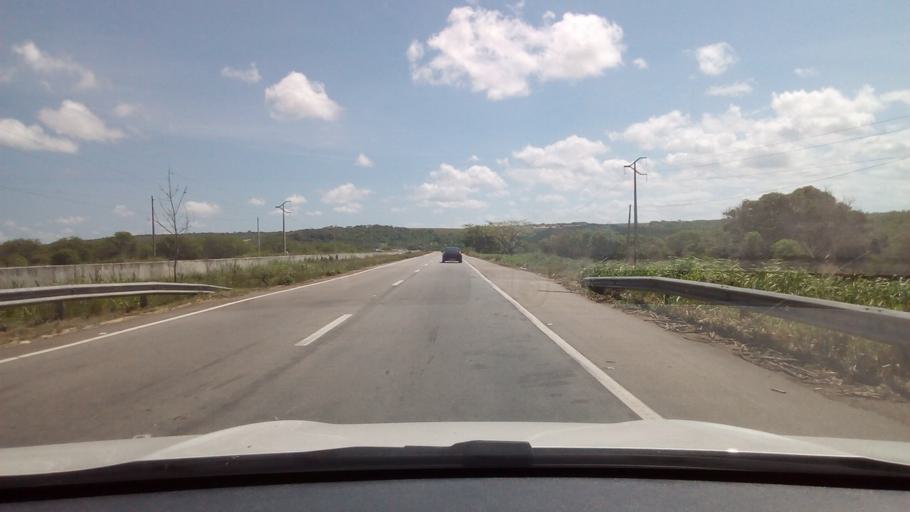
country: BR
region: Rio Grande do Norte
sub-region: Sao Jose De Mipibu
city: Sao Jose de Mipibu
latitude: -6.1010
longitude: -35.2343
